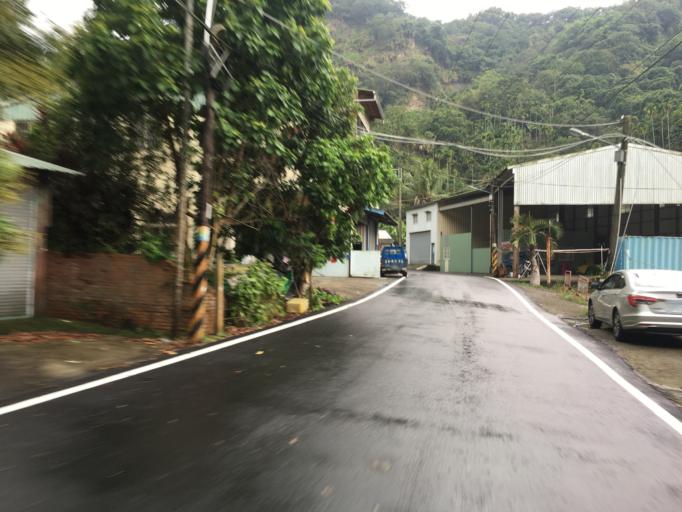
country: TW
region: Taiwan
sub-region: Taichung City
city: Taichung
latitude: 24.0596
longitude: 120.7415
